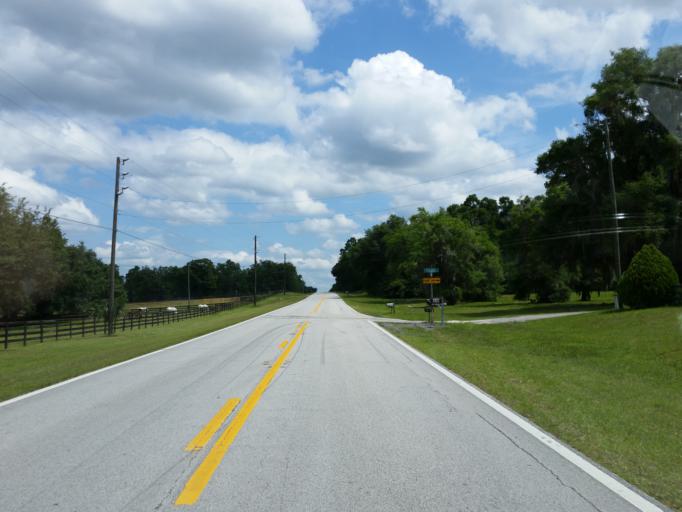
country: US
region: Florida
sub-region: Citrus County
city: Floral City
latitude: 28.6721
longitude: -82.3599
